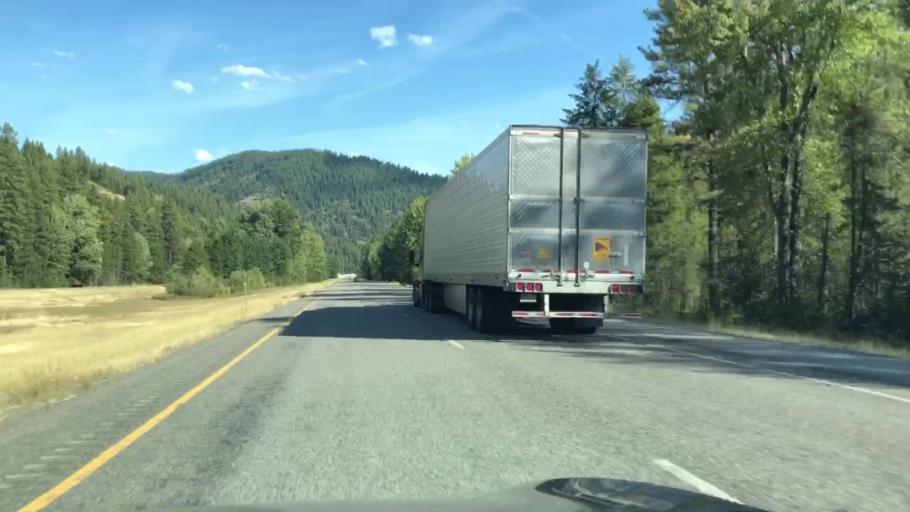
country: US
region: Montana
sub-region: Sanders County
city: Thompson Falls
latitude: 47.3591
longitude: -115.3129
